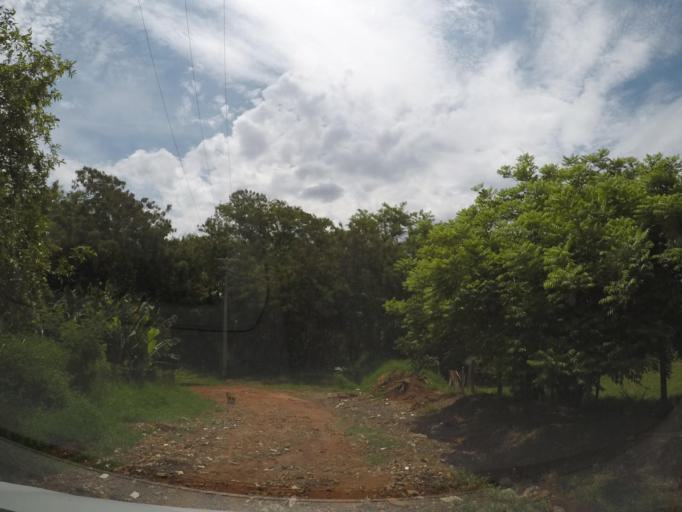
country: BR
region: Sao Paulo
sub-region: Sumare
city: Sumare
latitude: -22.8482
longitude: -47.3005
